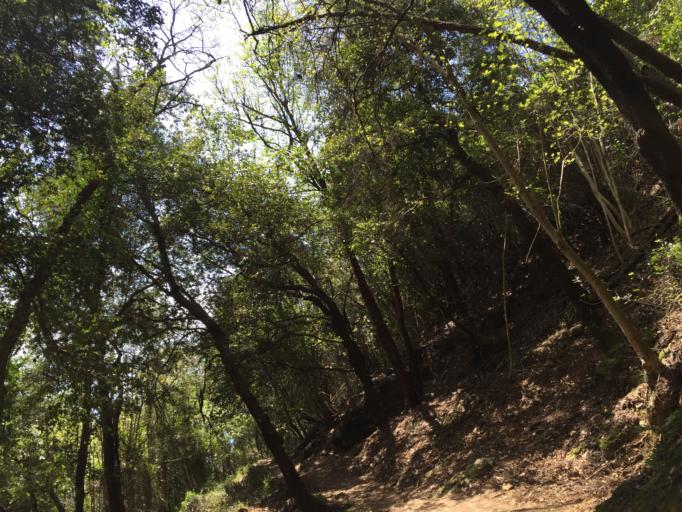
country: IT
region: Liguria
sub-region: Provincia di Genova
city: Portofino
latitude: 44.3214
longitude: 9.1781
